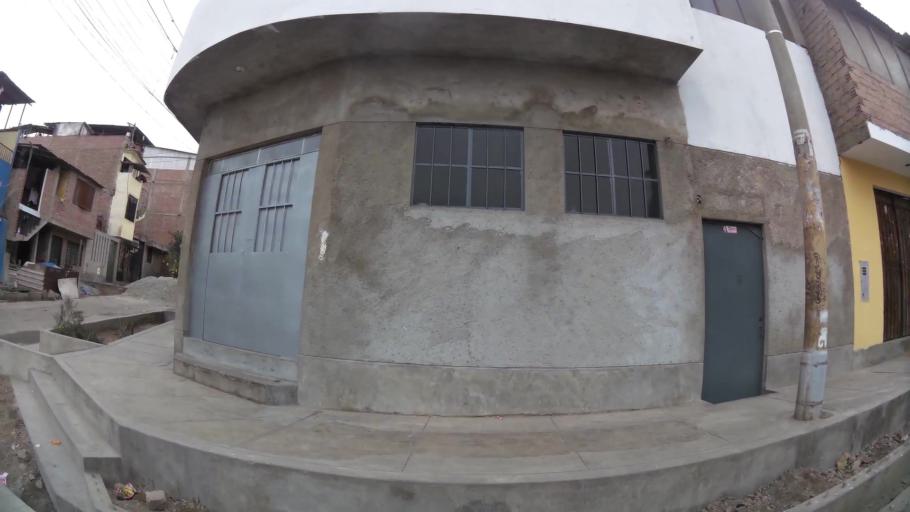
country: PE
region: Lima
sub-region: Lima
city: Surco
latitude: -12.1779
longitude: -76.9644
